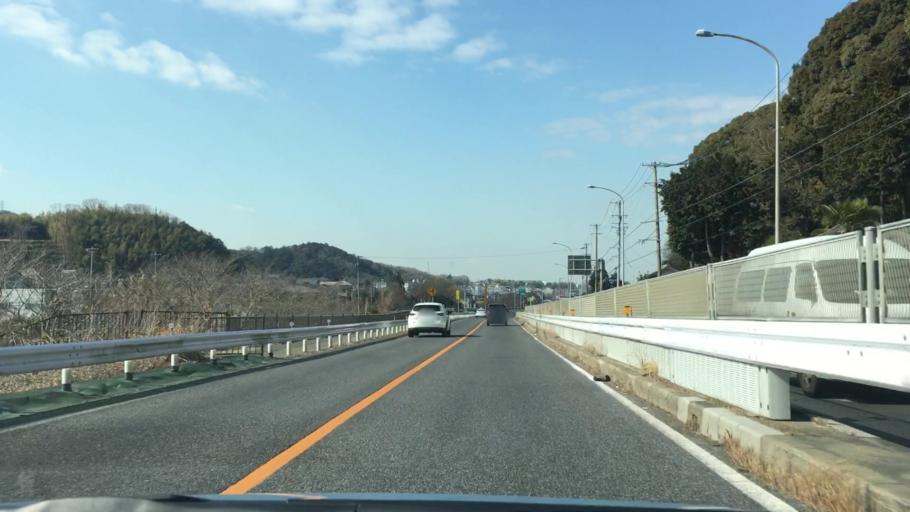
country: JP
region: Aichi
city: Okazaki
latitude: 34.9105
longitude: 137.2278
